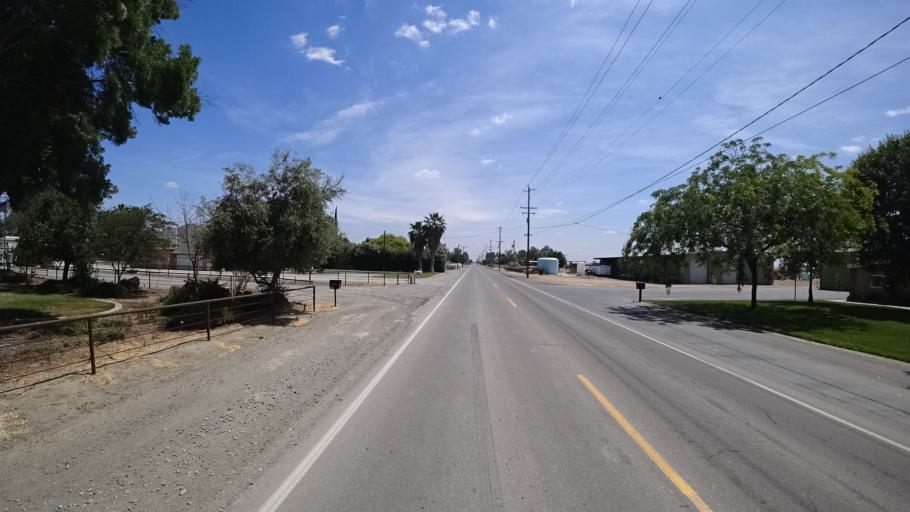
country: US
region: California
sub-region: Kings County
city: Home Garden
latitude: 36.2984
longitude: -119.6164
